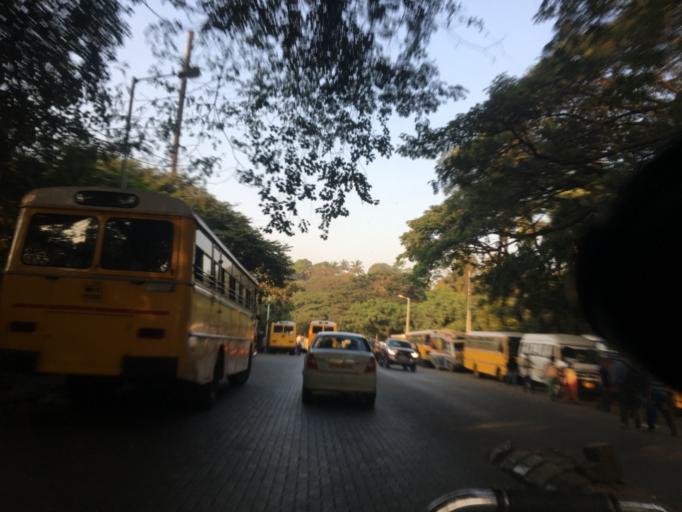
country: IN
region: Maharashtra
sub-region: Mumbai Suburban
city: Powai
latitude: 19.1301
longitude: 72.8967
